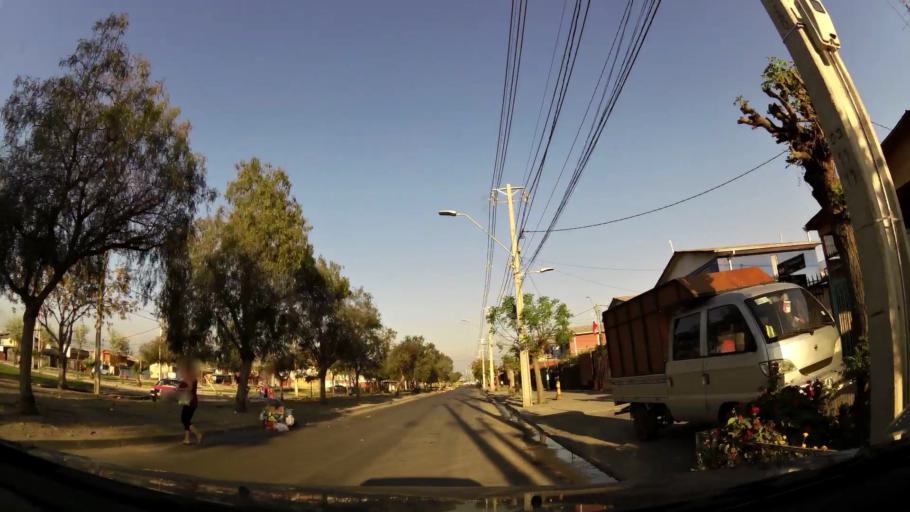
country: CL
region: Santiago Metropolitan
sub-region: Provincia de Maipo
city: San Bernardo
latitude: -33.5958
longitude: -70.6710
